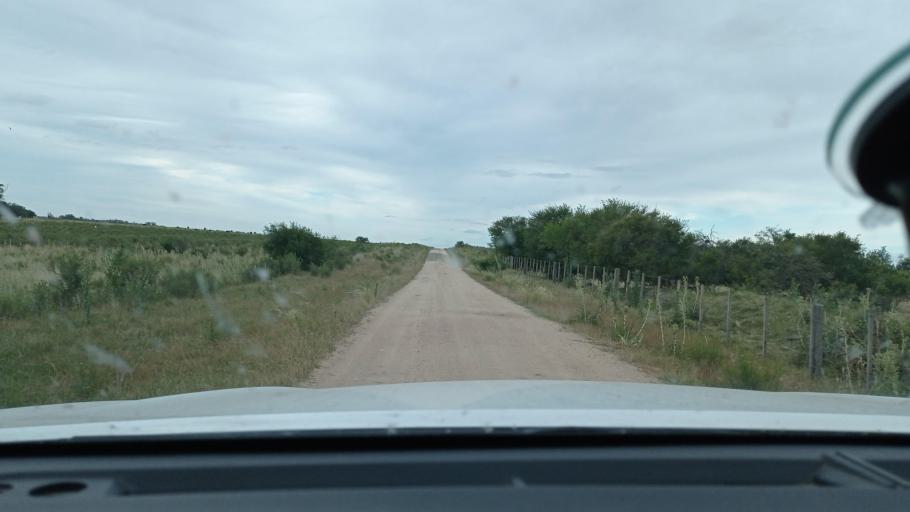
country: UY
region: Florida
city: Casupa
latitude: -34.1461
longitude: -55.7916
